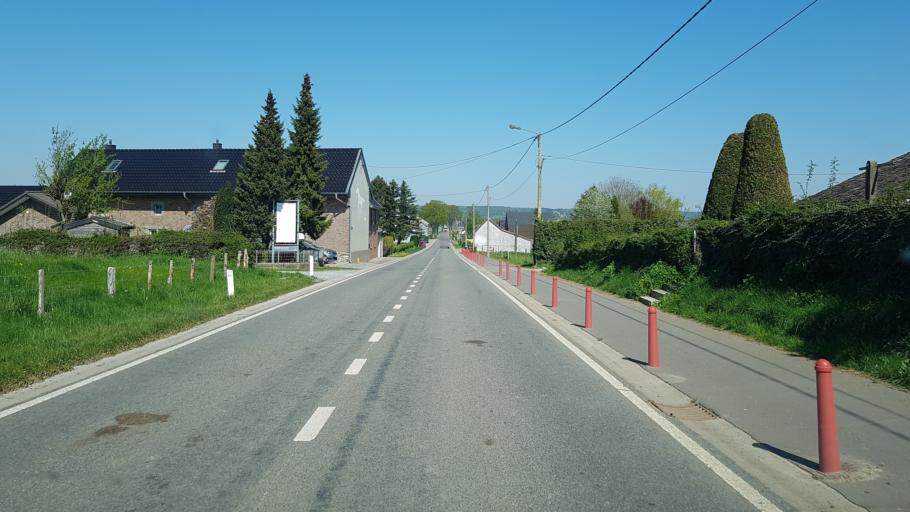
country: BE
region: Wallonia
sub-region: Province de Liege
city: Plombieres
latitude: 50.7283
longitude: 5.9321
